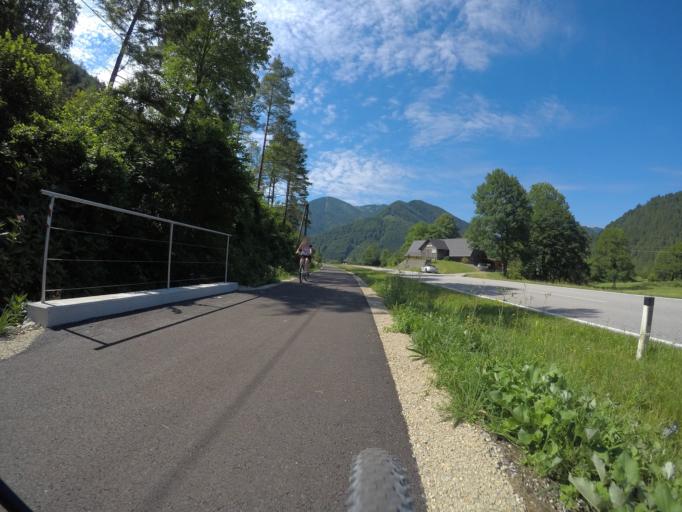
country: AT
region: Lower Austria
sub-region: Politischer Bezirk Amstetten
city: Hollenstein an der Ybbs
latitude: 47.8411
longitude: 14.7547
